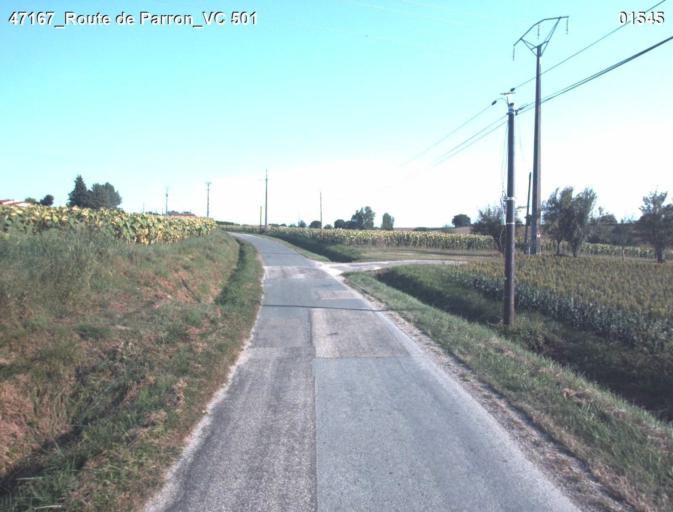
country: FR
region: Aquitaine
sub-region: Departement du Lot-et-Garonne
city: Mezin
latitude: 44.0485
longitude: 0.2638
